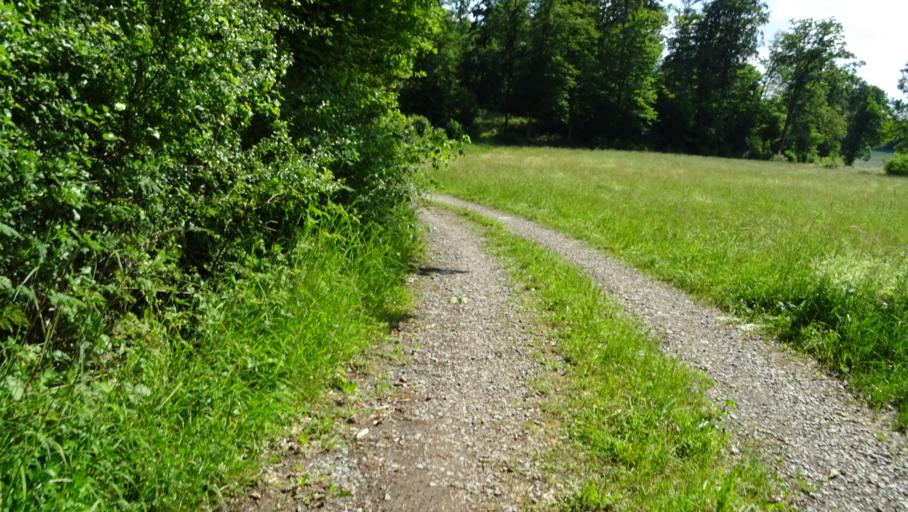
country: DE
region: Baden-Wuerttemberg
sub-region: Karlsruhe Region
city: Seckach
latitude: 49.4157
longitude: 9.3589
